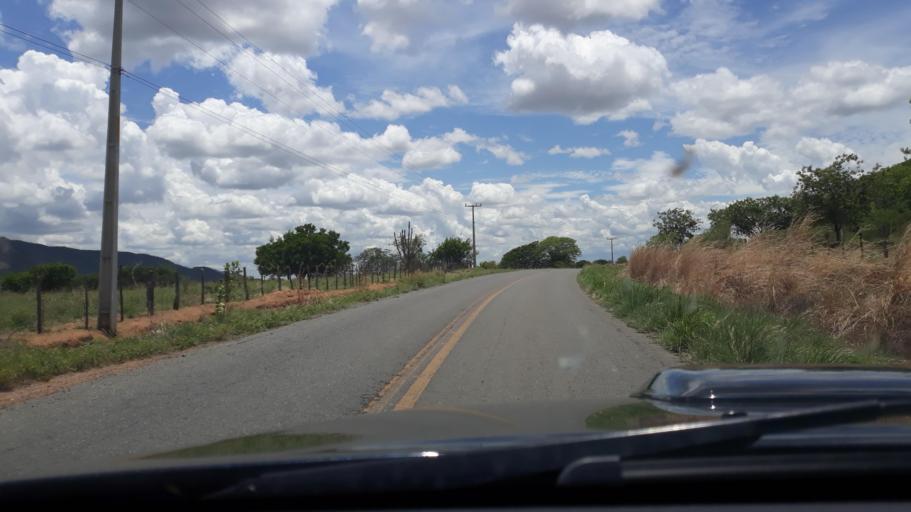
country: BR
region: Bahia
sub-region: Guanambi
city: Guanambi
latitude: -14.0477
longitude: -42.8728
